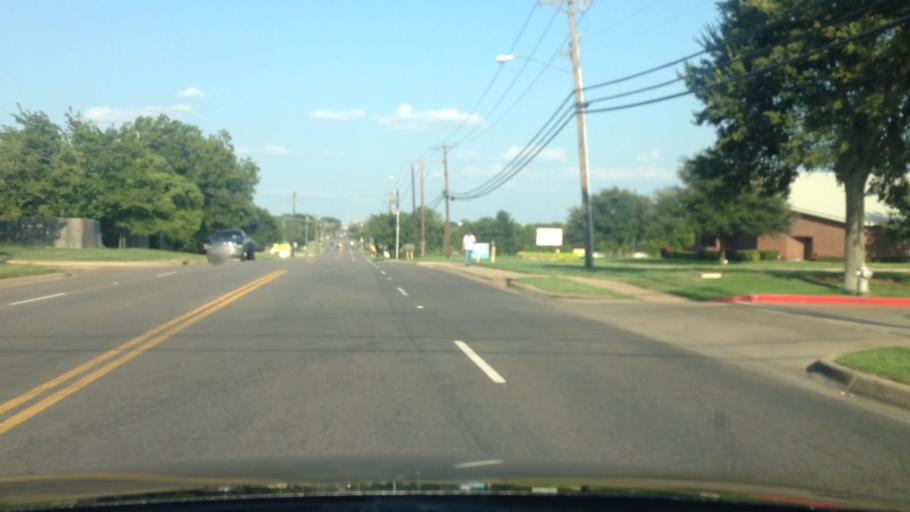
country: US
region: Texas
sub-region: Tarrant County
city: Edgecliff Village
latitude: 32.6352
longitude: -97.3381
